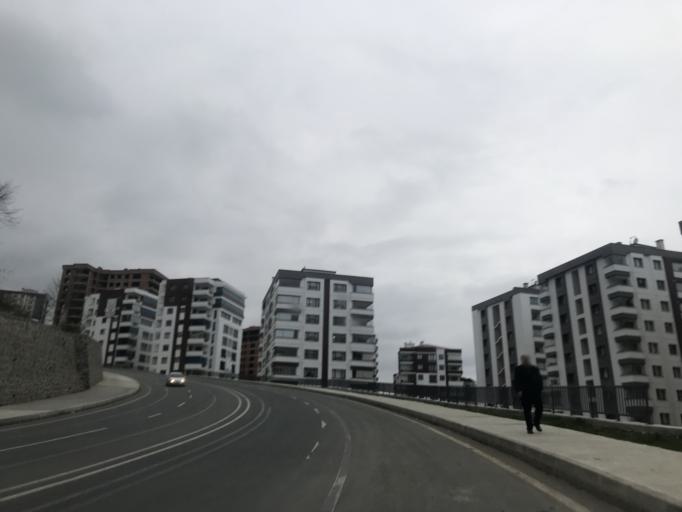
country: TR
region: Trabzon
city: Akcaabat
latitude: 41.0050
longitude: 39.6259
